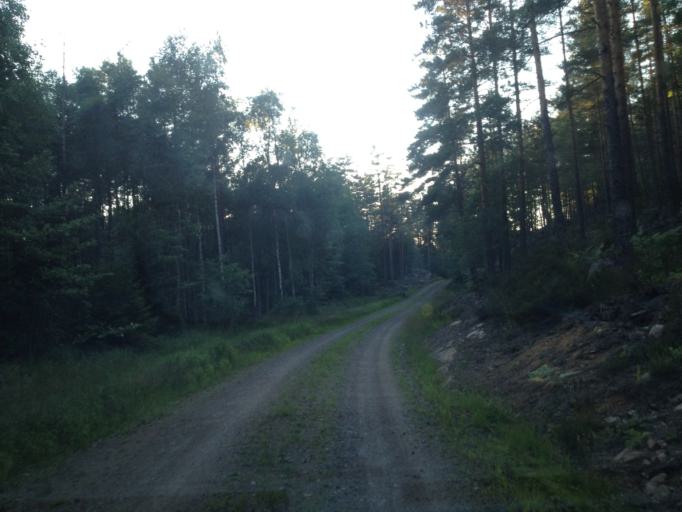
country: SE
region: Kalmar
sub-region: Vasterviks Kommun
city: Overum
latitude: 58.0000
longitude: 16.1549
